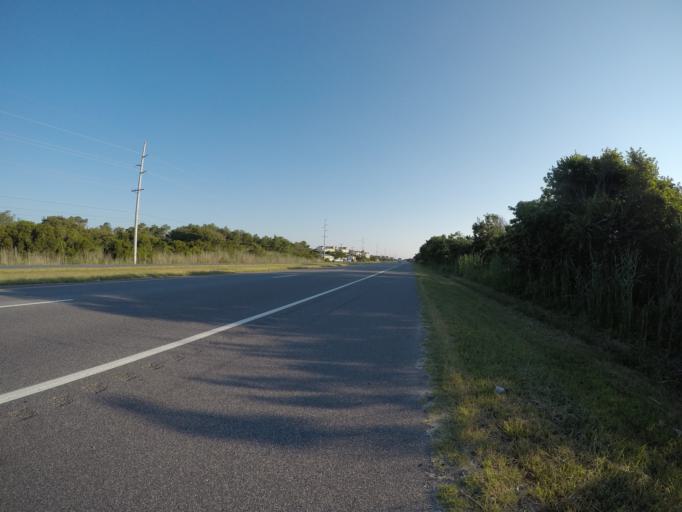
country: US
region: Delaware
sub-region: Sussex County
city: Bethany Beach
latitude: 38.4761
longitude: -75.0517
